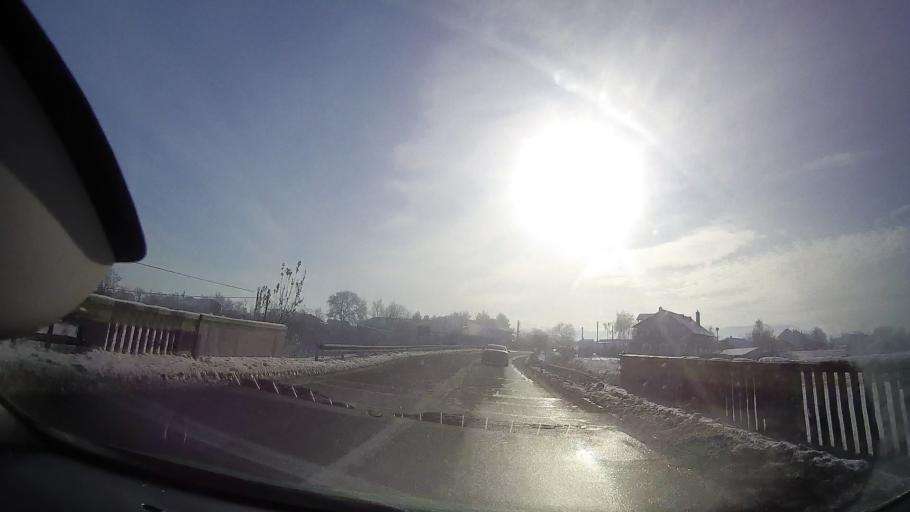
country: RO
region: Neamt
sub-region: Comuna Dobreni
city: Dobreni
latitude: 47.0032
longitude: 26.4237
